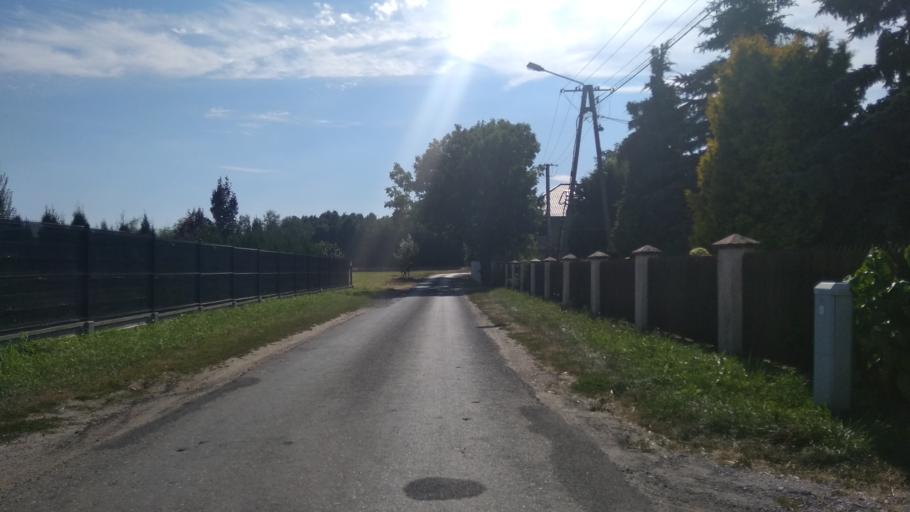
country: PL
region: Kujawsko-Pomorskie
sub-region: Powiat bydgoski
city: Osielsko
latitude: 53.2206
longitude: 18.1369
